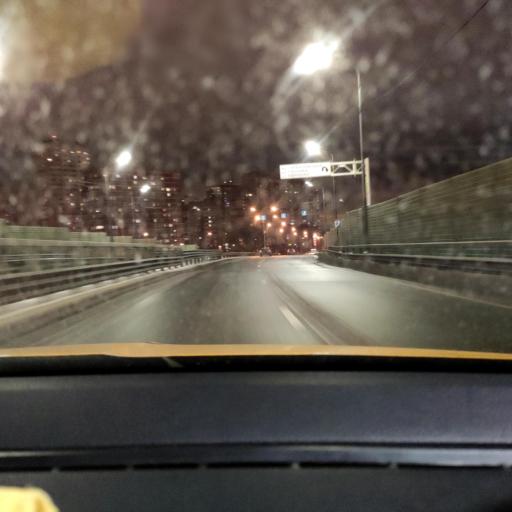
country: RU
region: Moskovskaya
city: Odintsovo
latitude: 55.6691
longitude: 37.2782
